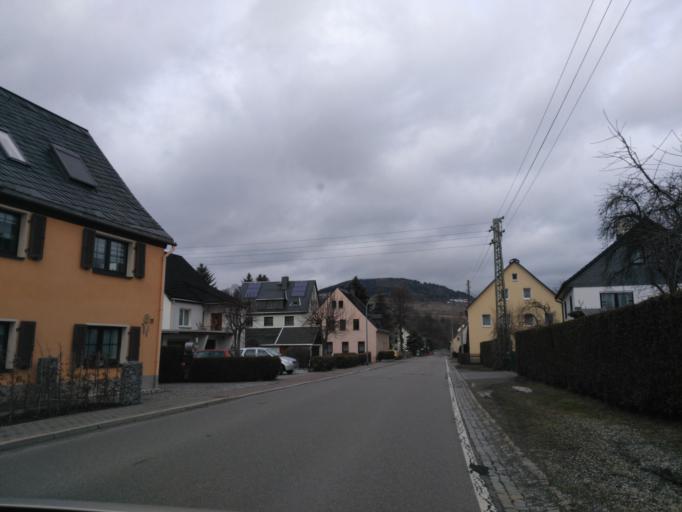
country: DE
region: Saxony
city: Konigswalde
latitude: 50.5506
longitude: 13.0456
